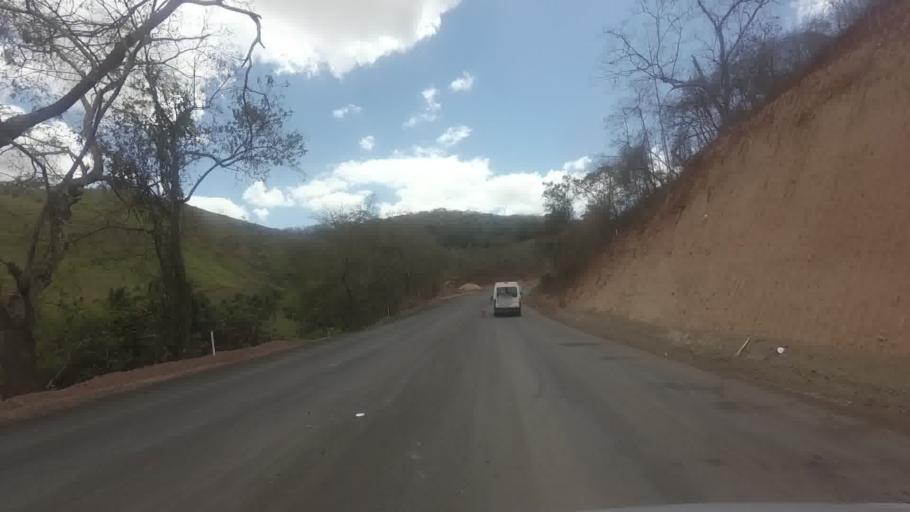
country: BR
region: Rio de Janeiro
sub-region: Santo Antonio De Padua
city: Santo Antonio de Padua
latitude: -21.5086
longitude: -42.0875
